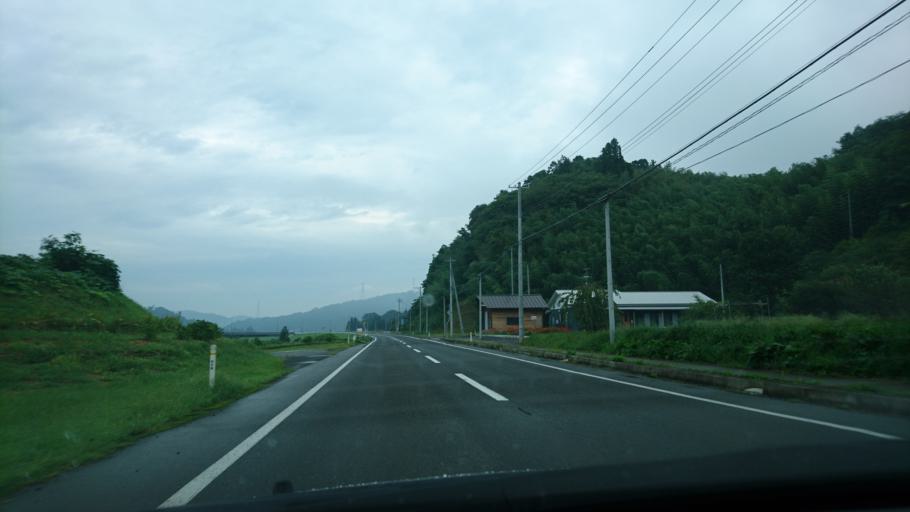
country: JP
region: Iwate
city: Ichinoseki
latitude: 38.9146
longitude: 141.2572
